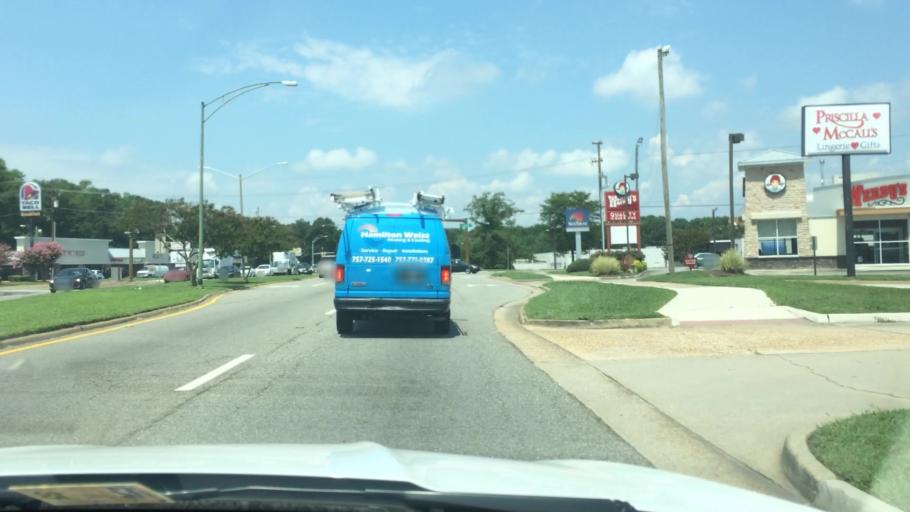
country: US
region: Virginia
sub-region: York County
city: Yorktown
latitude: 37.1295
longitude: -76.5376
